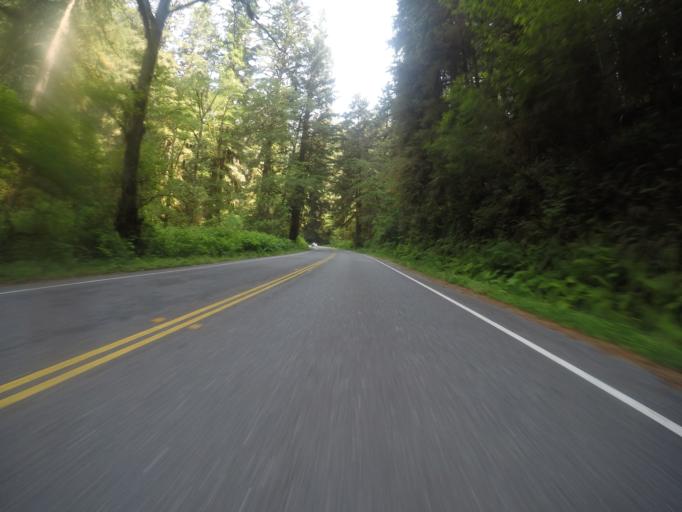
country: US
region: California
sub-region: Del Norte County
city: Bertsch-Oceanview
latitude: 41.4329
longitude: -124.0385
